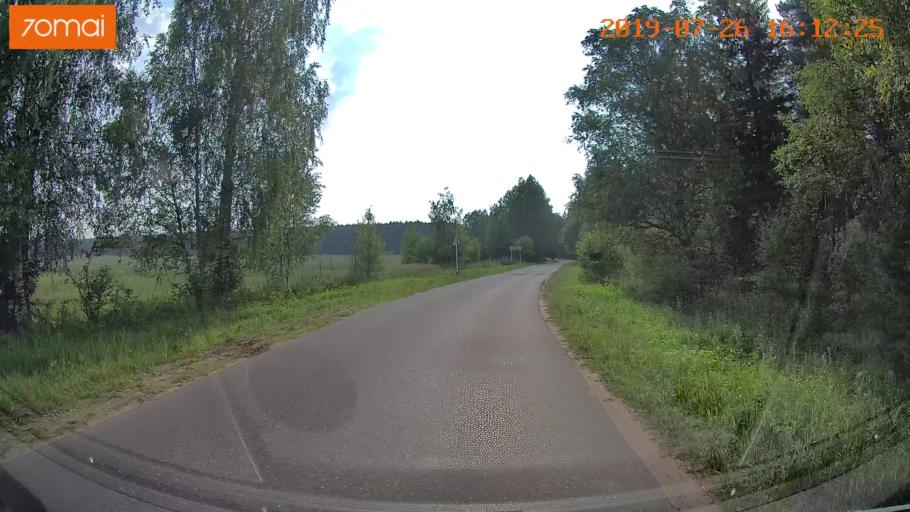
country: RU
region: Ivanovo
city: Bogorodskoye
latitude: 57.0686
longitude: 41.0498
